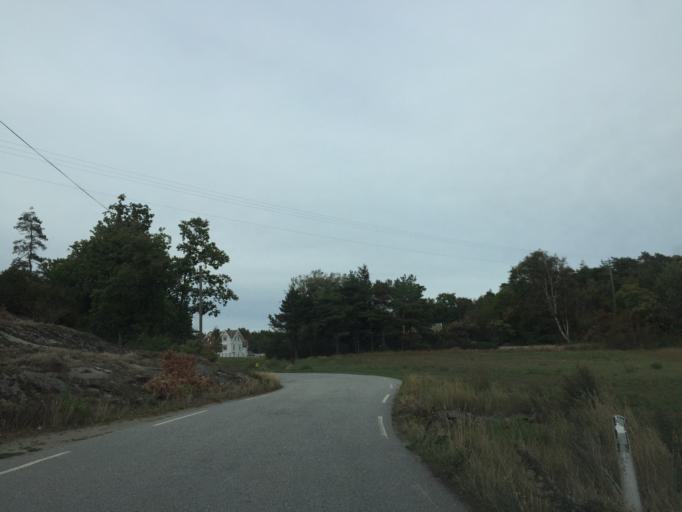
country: NO
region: Ostfold
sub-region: Hvaler
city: Skjaerhalden
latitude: 59.0485
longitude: 11.0440
